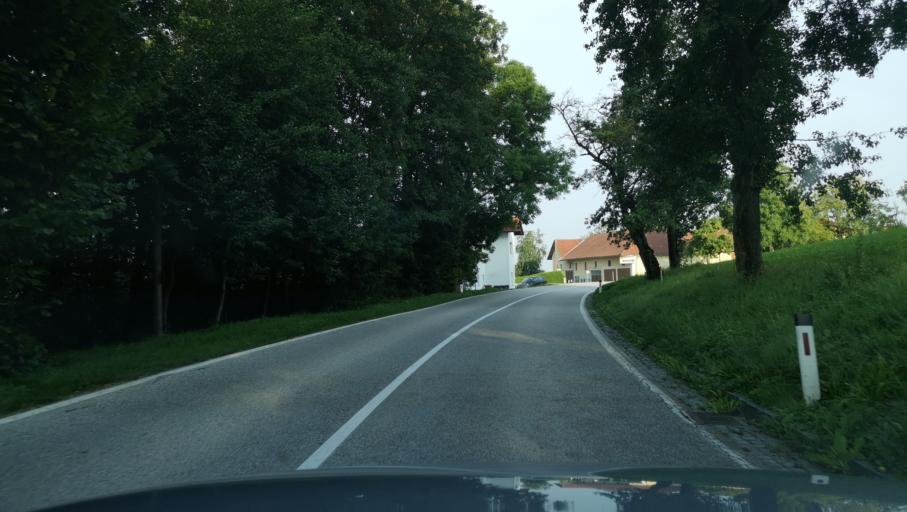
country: AT
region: Upper Austria
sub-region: Politischer Bezirk Grieskirchen
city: Grieskirchen
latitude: 48.3502
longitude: 13.7382
